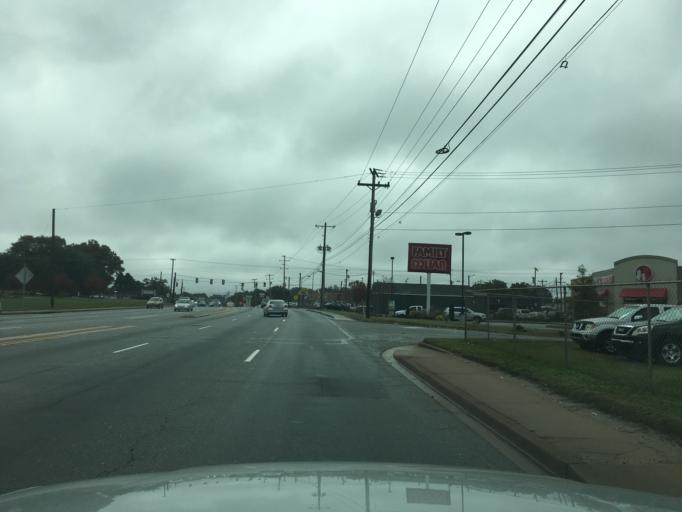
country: US
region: South Carolina
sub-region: Greenville County
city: Welcome
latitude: 34.8213
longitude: -82.4457
